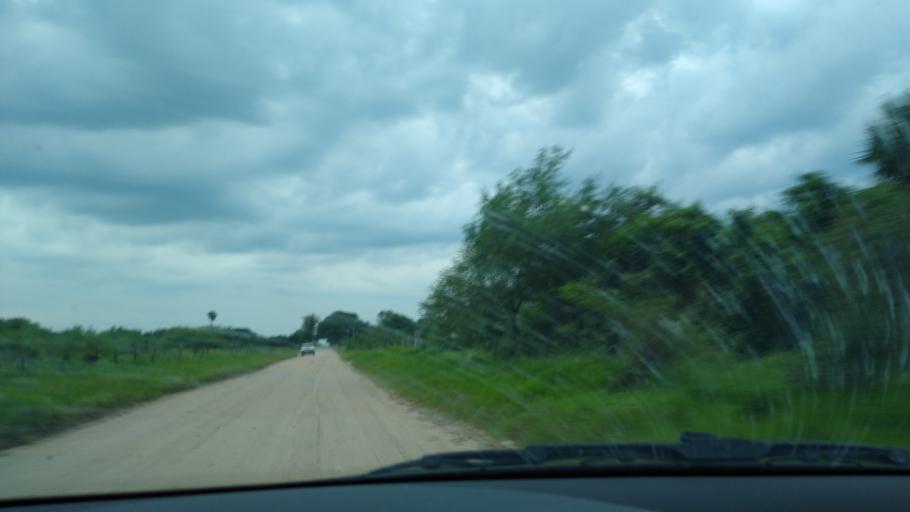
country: AR
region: Chaco
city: Puerto Vilelas
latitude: -27.5107
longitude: -58.9673
